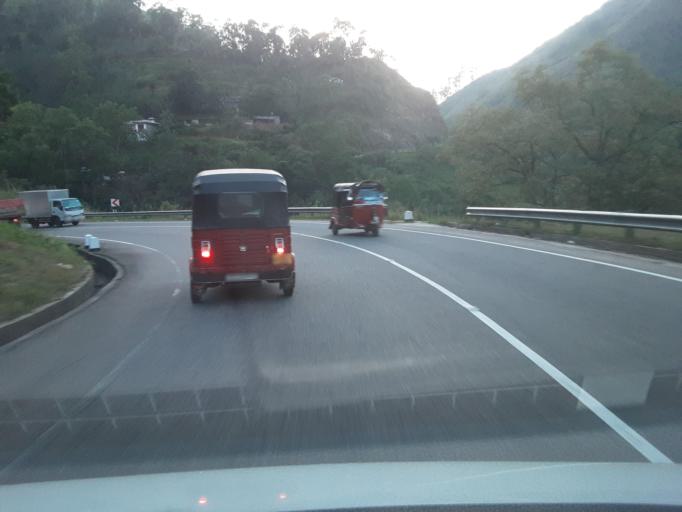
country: LK
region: Uva
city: Badulla
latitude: 6.9156
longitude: 80.9553
